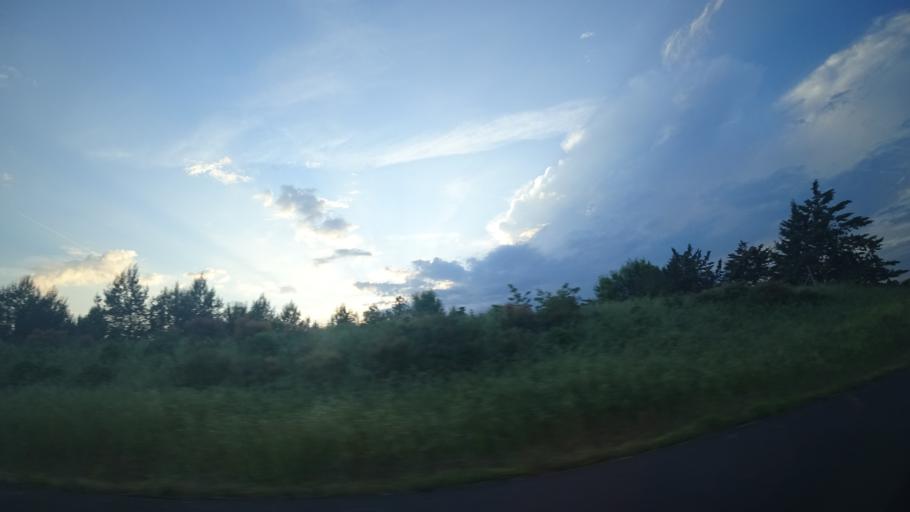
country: FR
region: Languedoc-Roussillon
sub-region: Departement de l'Herault
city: Lezignan-la-Cebe
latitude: 43.4842
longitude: 3.4385
